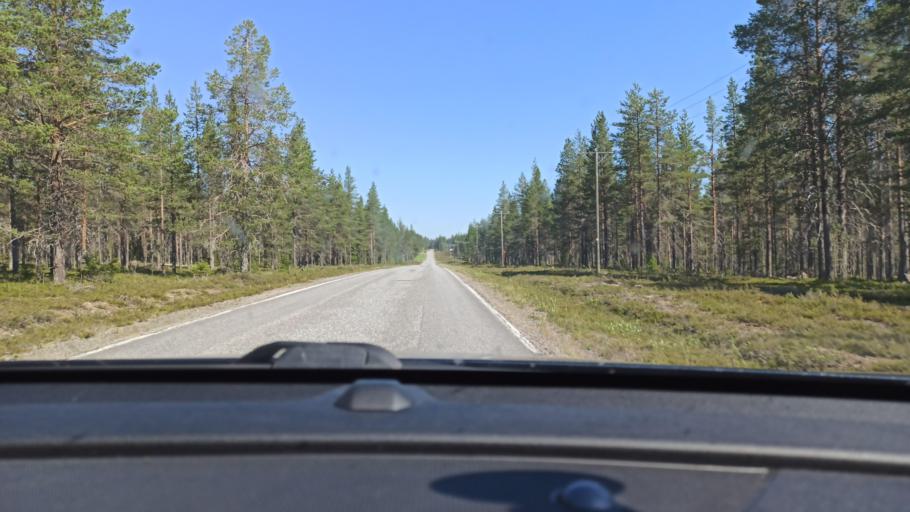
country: FI
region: Lapland
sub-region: Tunturi-Lappi
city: Kolari
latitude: 67.6493
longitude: 24.1615
